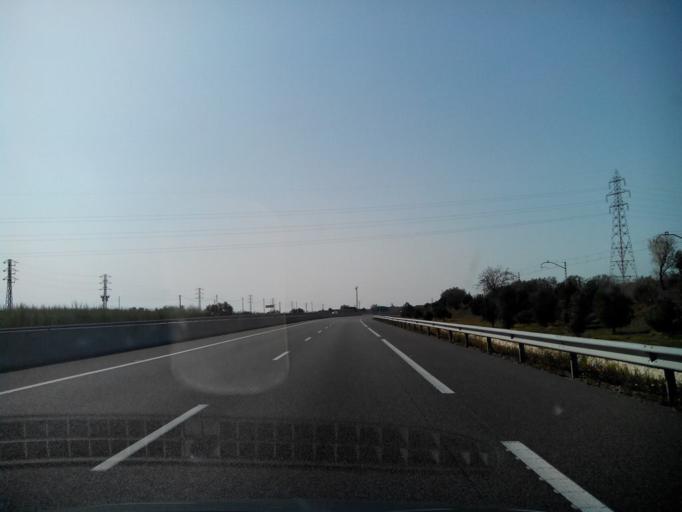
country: ES
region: Catalonia
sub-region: Provincia de Tarragona
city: La Selva
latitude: 41.2297
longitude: 1.1619
